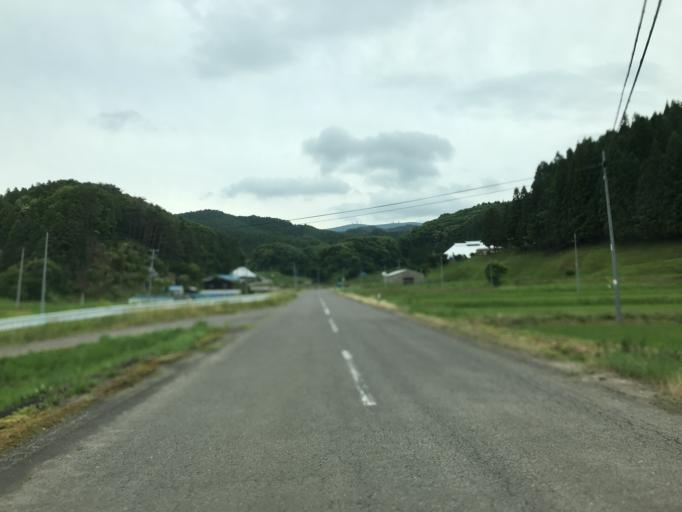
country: JP
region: Fukushima
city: Funehikimachi-funehiki
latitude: 37.3977
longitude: 140.6641
